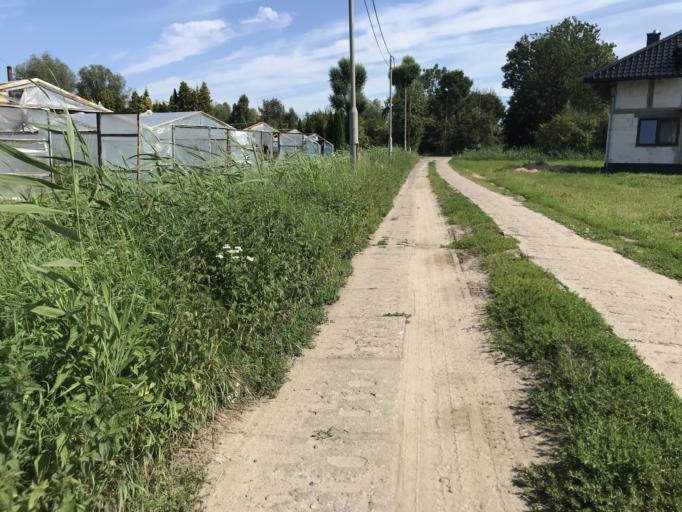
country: PL
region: Pomeranian Voivodeship
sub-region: Gdansk
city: Gdansk
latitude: 54.3208
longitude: 18.6779
